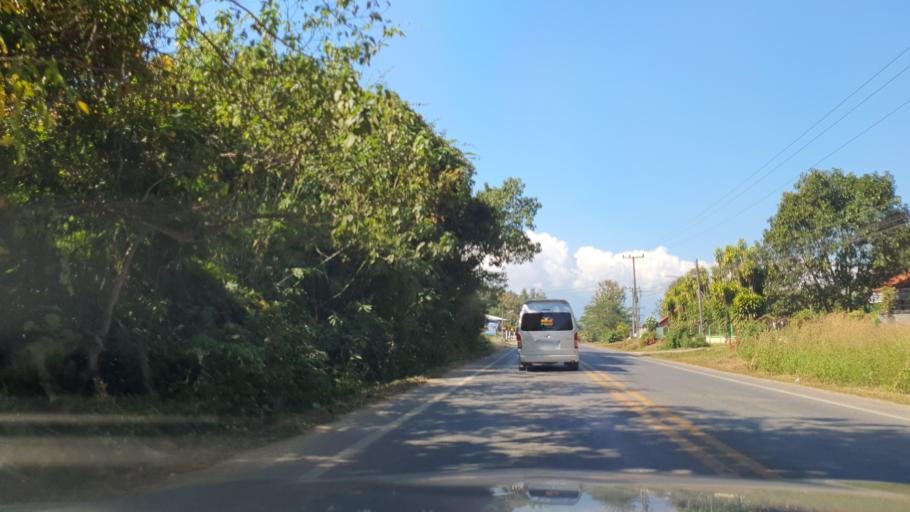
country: TH
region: Nan
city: Tha Wang Pha
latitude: 19.1029
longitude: 100.8230
